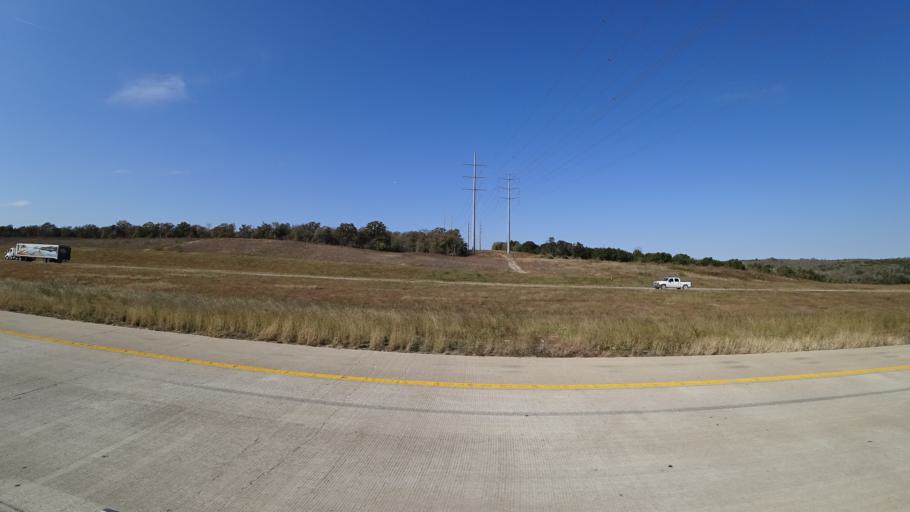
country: US
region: Texas
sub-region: Travis County
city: Hornsby Bend
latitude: 30.2918
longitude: -97.5730
